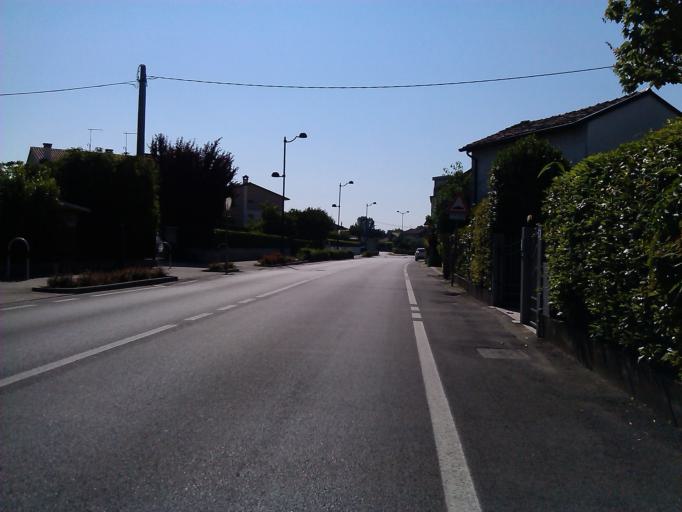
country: IT
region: Veneto
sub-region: Provincia di Vicenza
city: San Zeno-San Giuseppe
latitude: 45.7609
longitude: 11.7647
